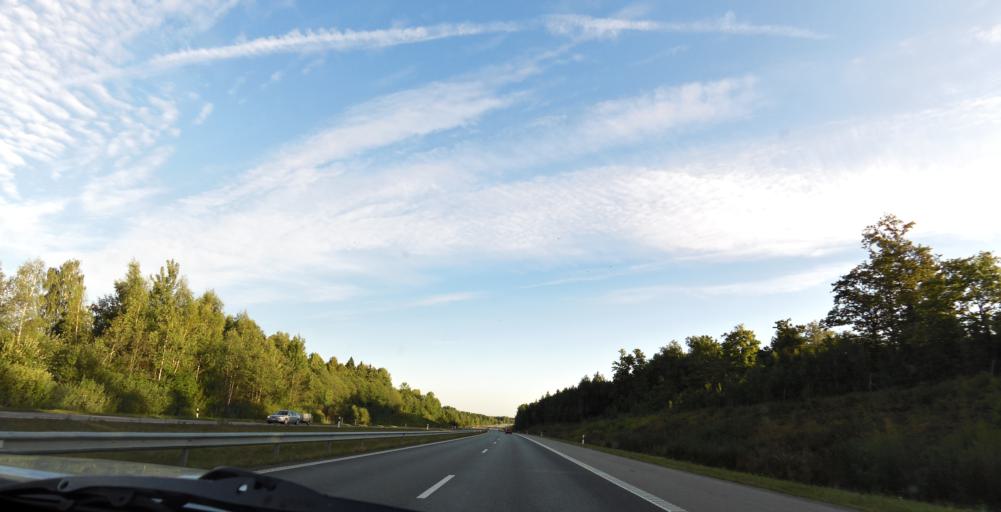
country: LT
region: Vilnius County
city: Ukmerge
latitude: 55.2122
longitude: 24.8172
